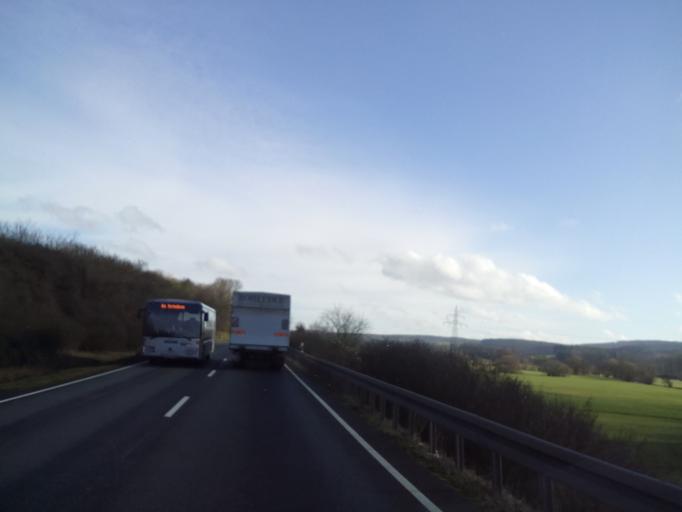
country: DE
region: Bavaria
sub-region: Upper Franconia
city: Altenkunstadt
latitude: 50.1299
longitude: 11.2619
